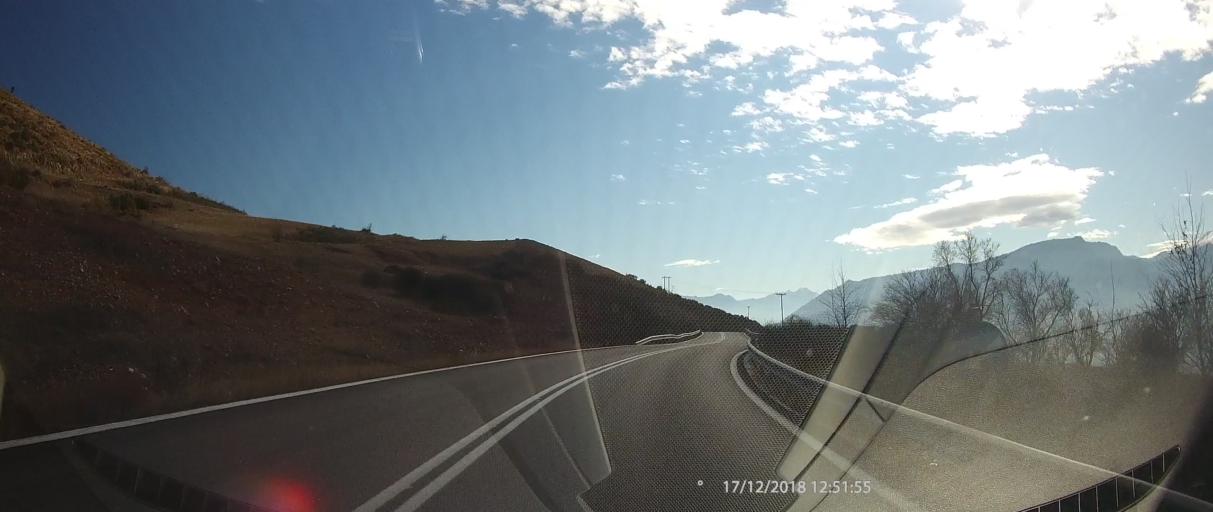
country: GR
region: Thessaly
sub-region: Trikala
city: Kastraki
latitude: 39.7612
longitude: 21.4735
